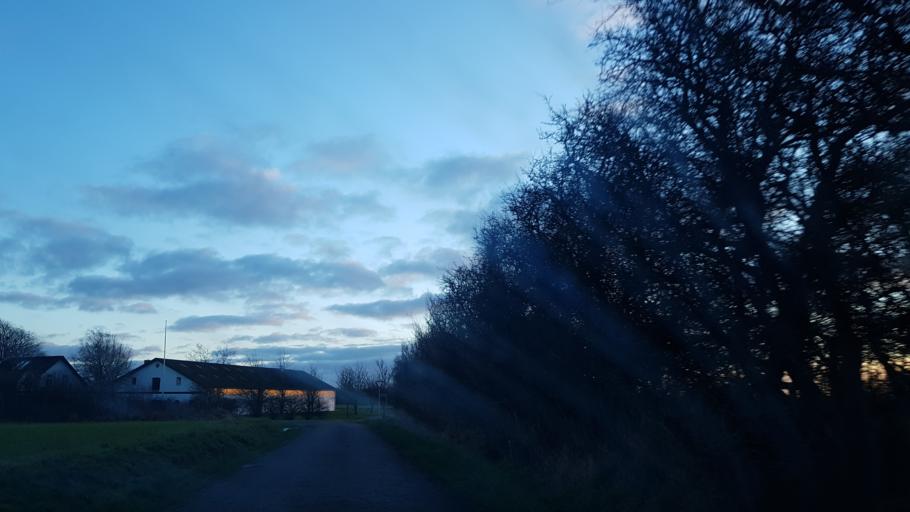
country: DK
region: South Denmark
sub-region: Kolding Kommune
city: Vamdrup
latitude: 55.3415
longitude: 9.2531
